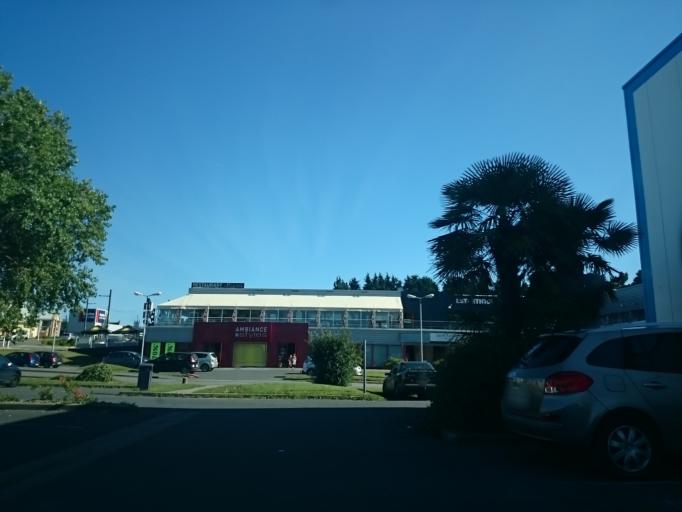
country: FR
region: Brittany
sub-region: Departement du Finistere
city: Gouesnou
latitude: 48.4246
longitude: -4.4676
